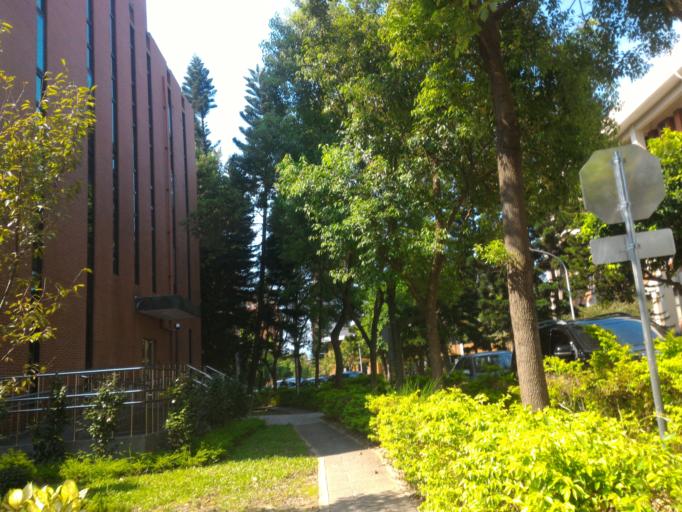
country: TW
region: Taipei
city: Taipei
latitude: 25.0418
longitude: 121.6158
